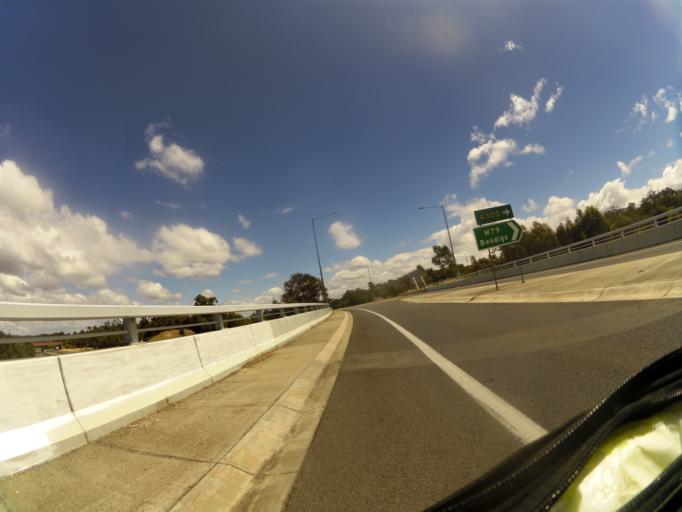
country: AU
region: Victoria
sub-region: Mount Alexander
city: Castlemaine
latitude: -37.0038
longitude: 144.2494
